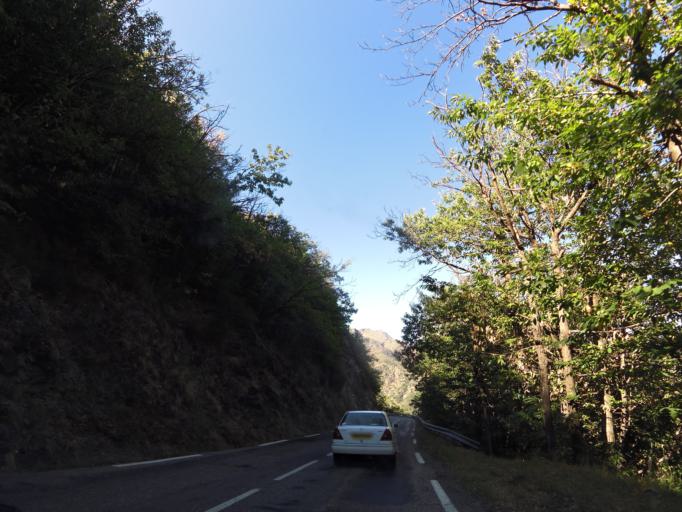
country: FR
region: Languedoc-Roussillon
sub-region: Departement du Gard
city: Valleraugue
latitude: 44.0871
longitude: 3.5775
